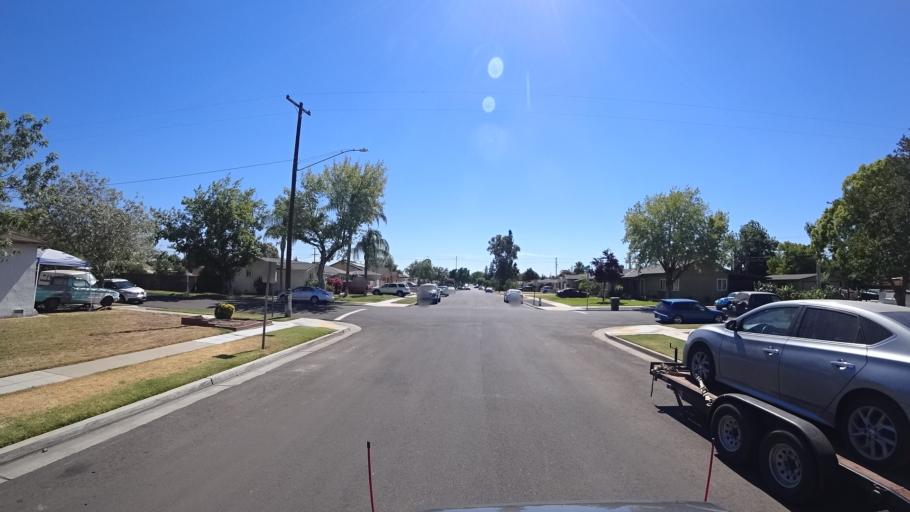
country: US
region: California
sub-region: Fresno County
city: Fresno
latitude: 36.7838
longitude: -119.8291
